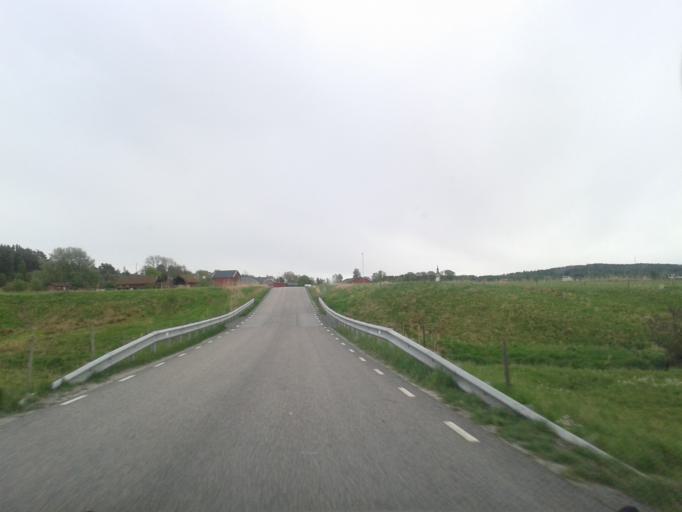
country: SE
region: Vaestra Goetaland
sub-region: Kungalvs Kommun
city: Kode
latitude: 57.9504
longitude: 11.8184
